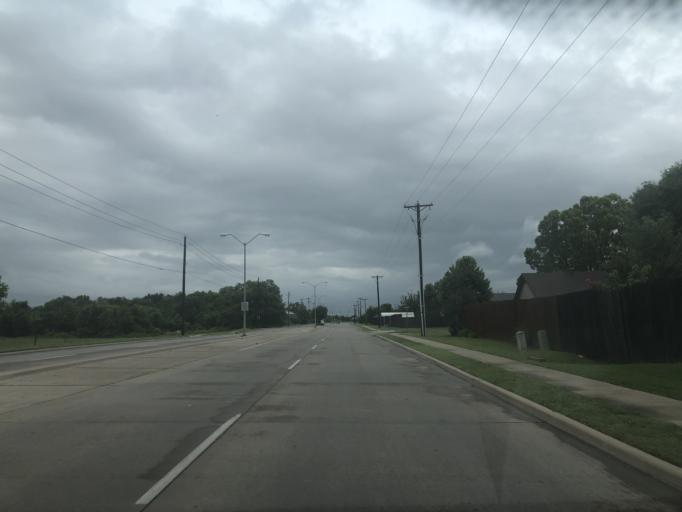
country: US
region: Texas
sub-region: Dallas County
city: Irving
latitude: 32.7901
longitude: -96.9598
